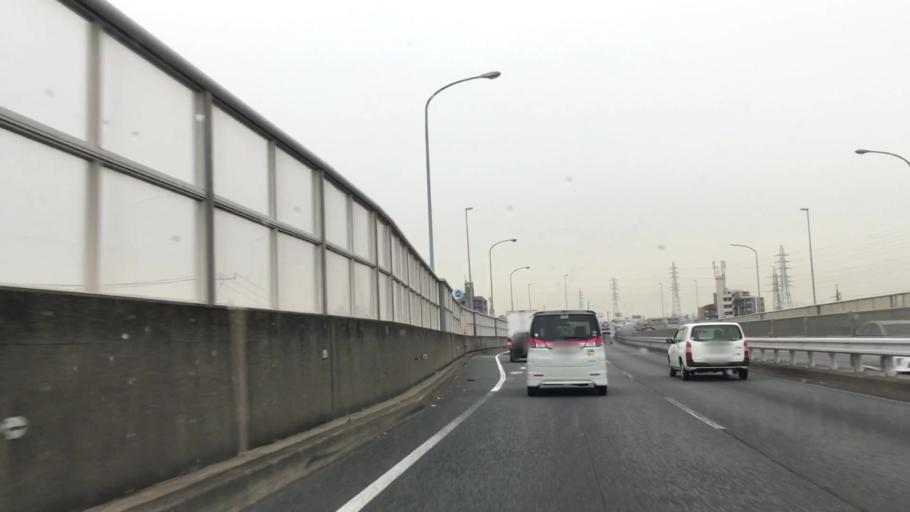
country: JP
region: Aichi
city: Chiryu
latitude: 35.0085
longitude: 137.0259
